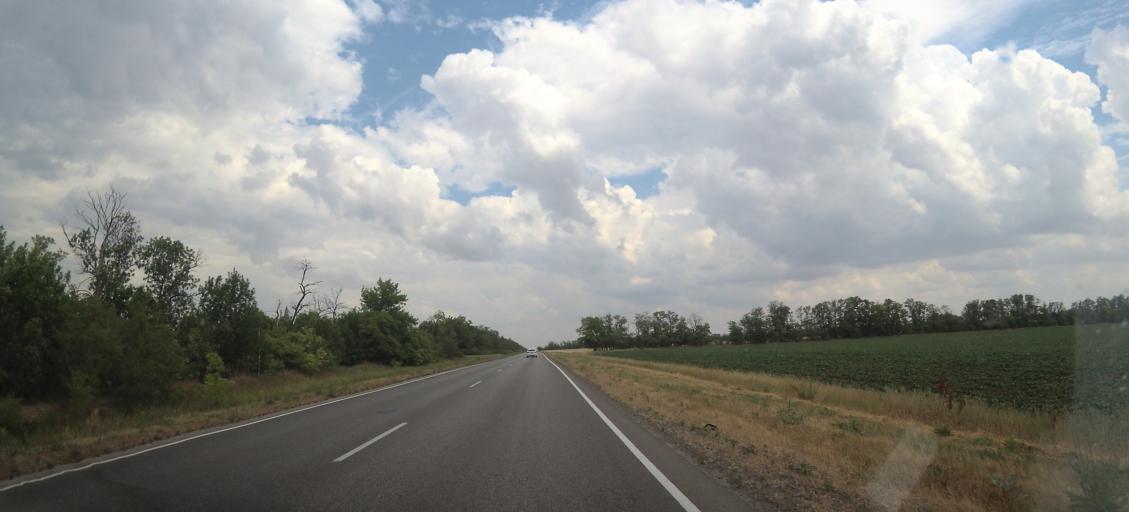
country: RU
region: Rostov
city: Peschanokopskoye
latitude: 46.0866
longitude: 41.0933
